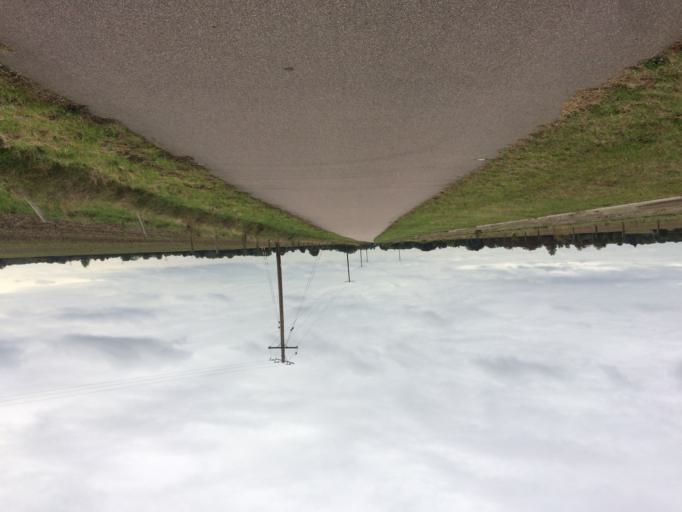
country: GB
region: England
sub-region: Cambridgeshire
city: Histon
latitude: 52.2610
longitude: 0.0811
